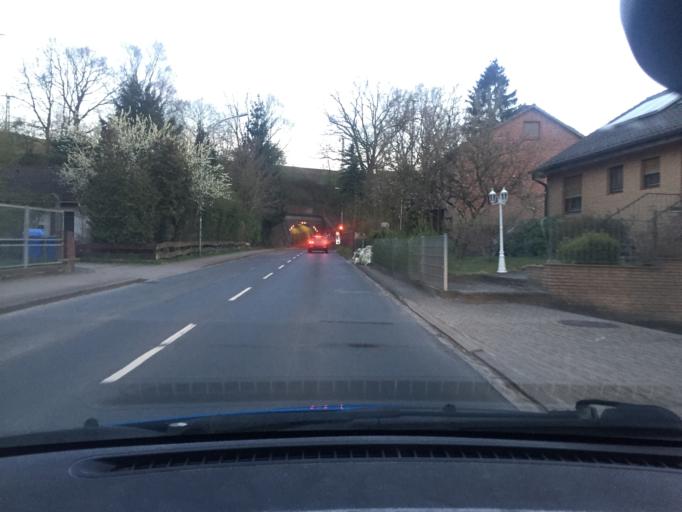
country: DE
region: Lower Saxony
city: Buchholz in der Nordheide
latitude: 53.3236
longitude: 9.8579
